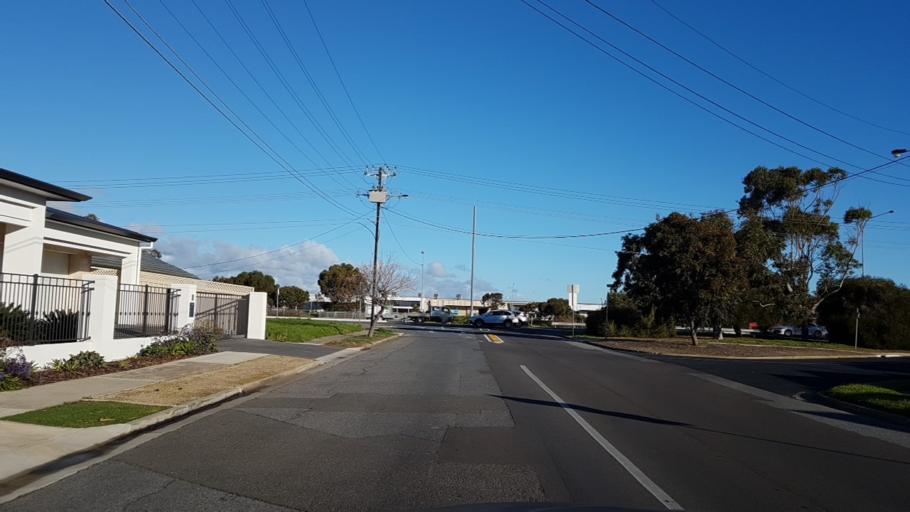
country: AU
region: South Australia
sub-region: City of West Torrens
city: Plympton
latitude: -34.9333
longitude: 138.5242
